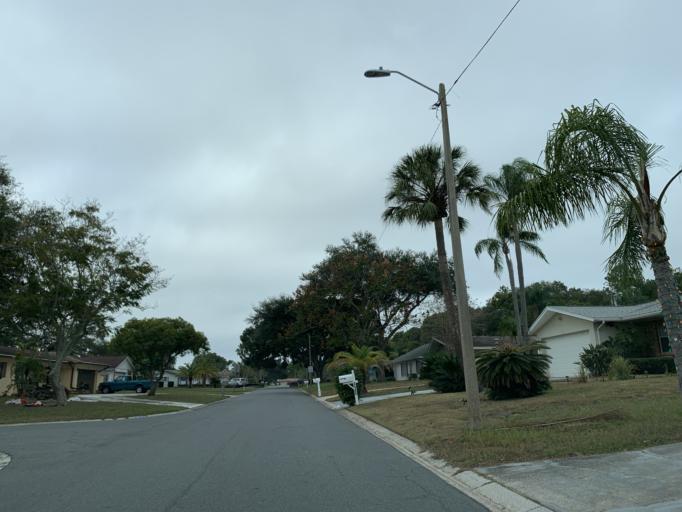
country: US
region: Florida
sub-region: Pinellas County
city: South Highpoint
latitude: 27.9529
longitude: -82.7345
